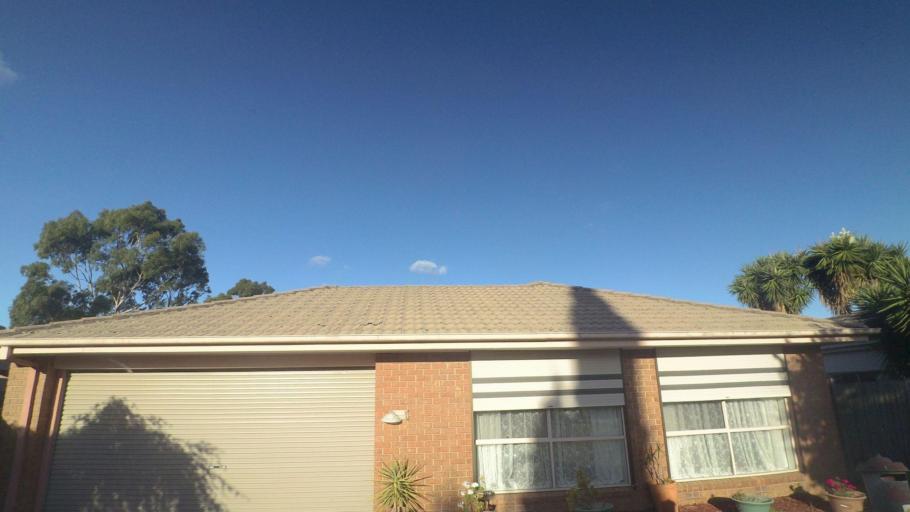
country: AU
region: Victoria
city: Burwood East
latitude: -37.8586
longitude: 145.1642
